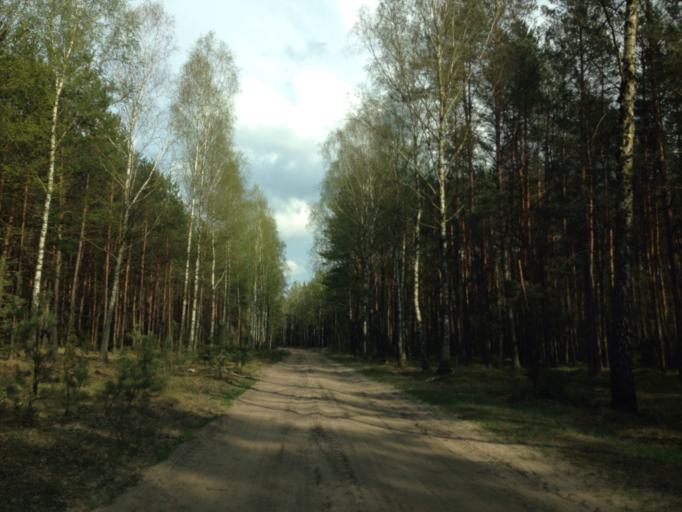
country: PL
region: Kujawsko-Pomorskie
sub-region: Powiat brodnicki
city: Gorzno
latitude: 53.1255
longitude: 19.6906
